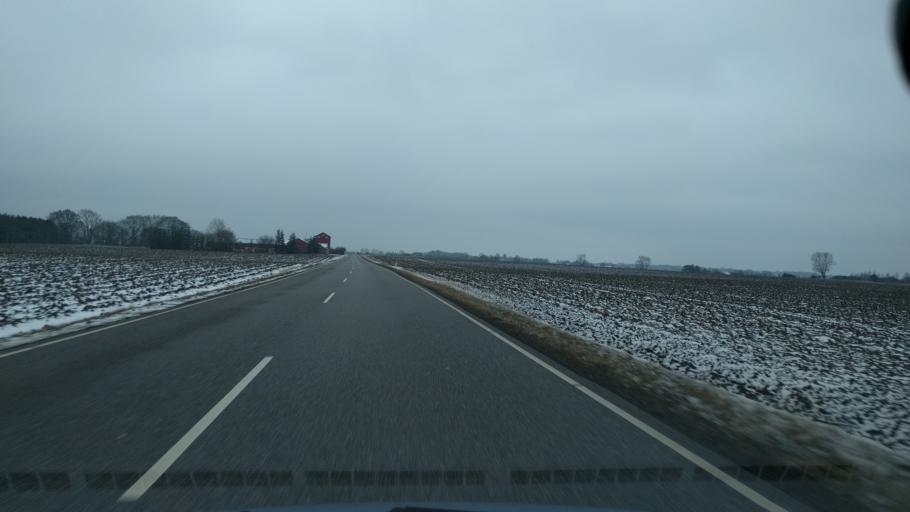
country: DK
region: Zealand
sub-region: Guldborgsund Kommune
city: Nykobing Falster
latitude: 54.7851
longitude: 11.9863
